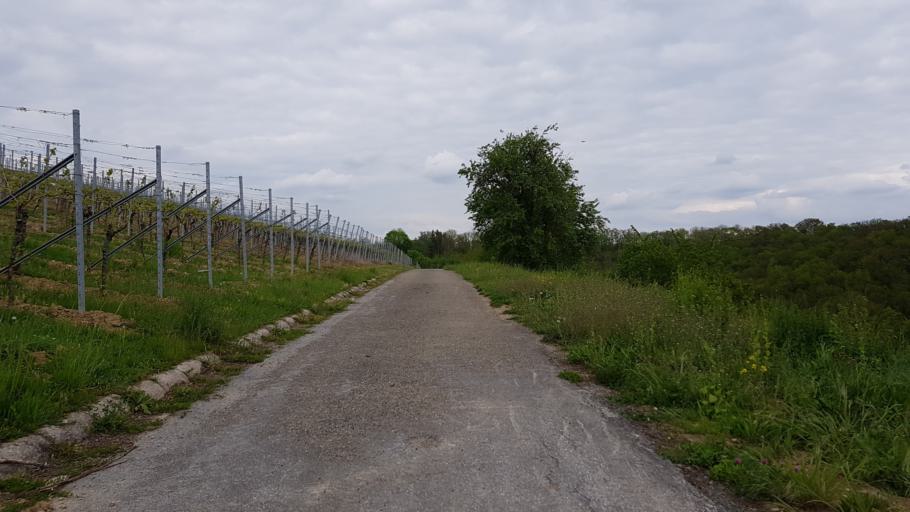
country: DE
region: Baden-Wuerttemberg
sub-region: Regierungsbezirk Stuttgart
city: Steinheim am der Murr
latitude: 48.9612
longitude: 9.2937
